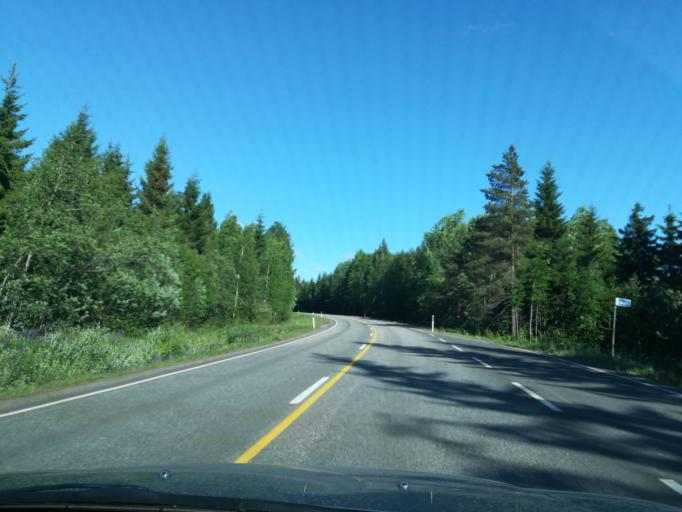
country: FI
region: South Karelia
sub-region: Imatra
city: Ruokolahti
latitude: 61.3515
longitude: 28.7354
